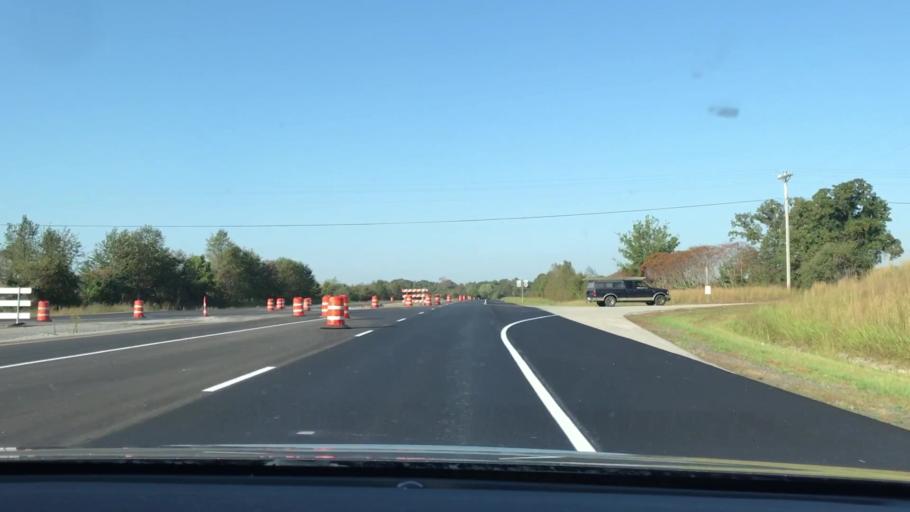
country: US
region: Kentucky
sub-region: Trigg County
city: Cadiz
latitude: 36.8391
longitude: -87.8424
